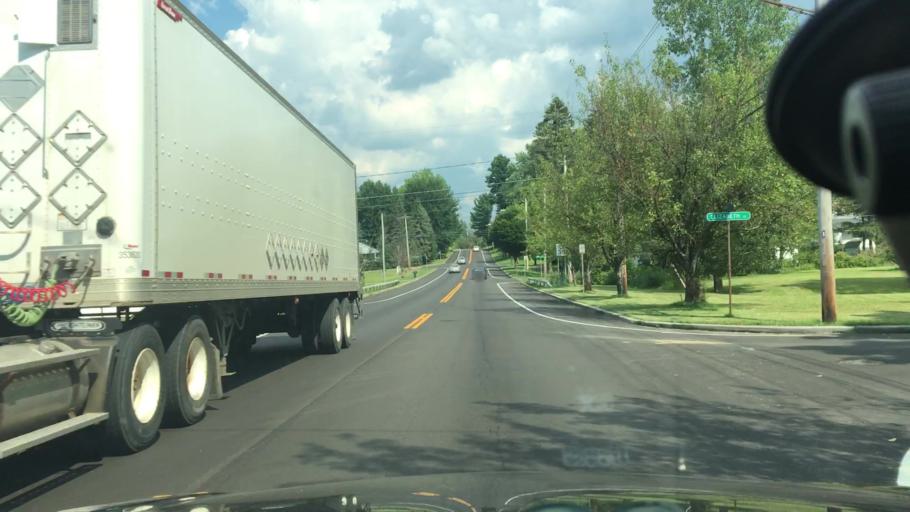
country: US
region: New York
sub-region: Chautauqua County
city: Lakewood
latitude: 42.0979
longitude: -79.3332
